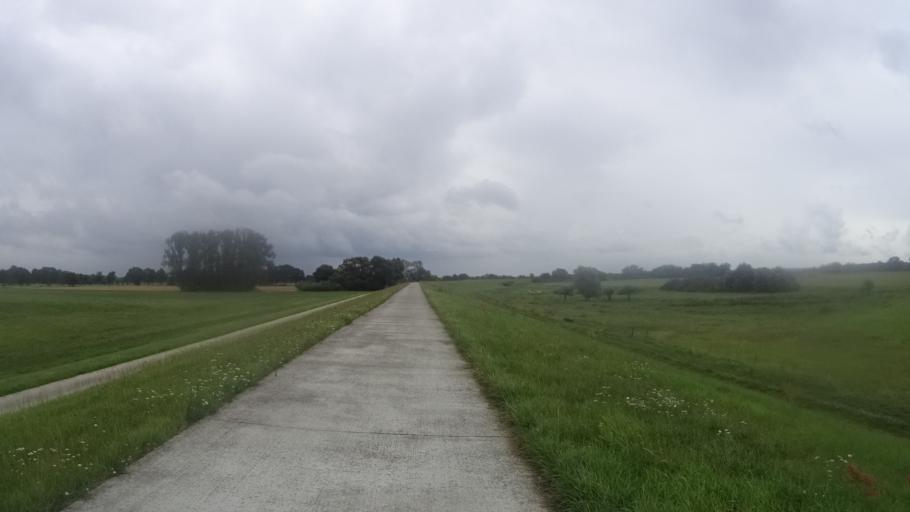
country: DE
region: Lower Saxony
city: Bleckede
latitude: 53.2985
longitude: 10.7807
